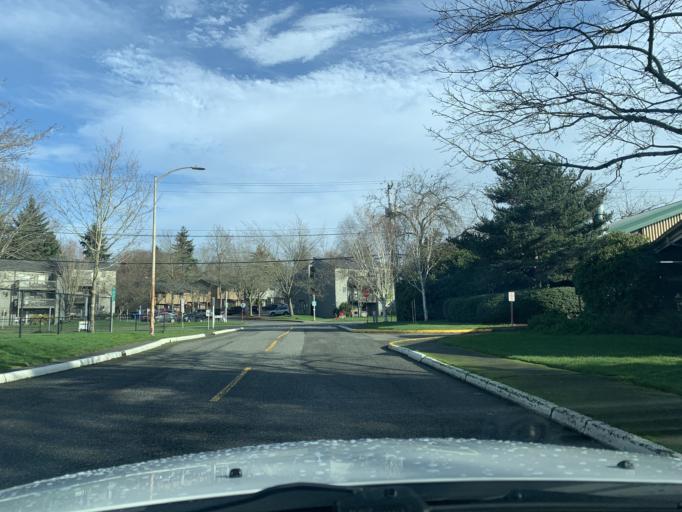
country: US
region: Washington
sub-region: King County
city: Seattle
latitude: 47.6601
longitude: -122.2928
